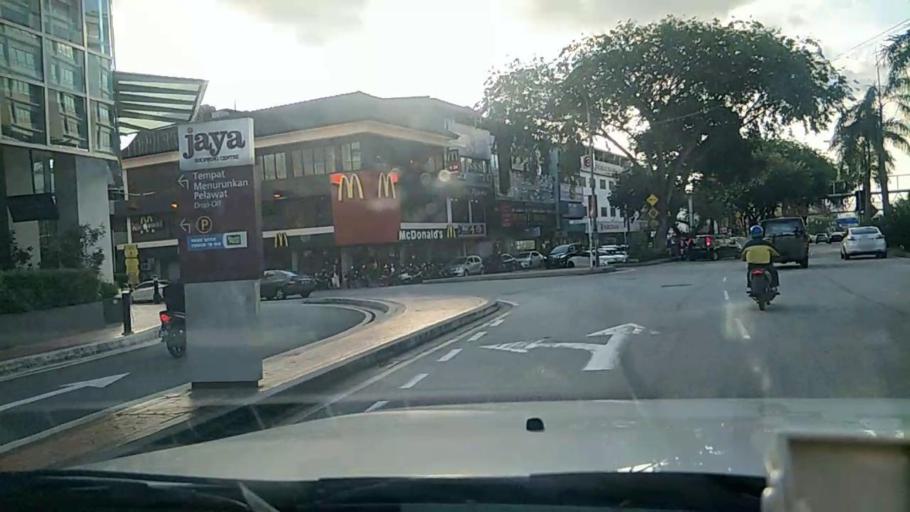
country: MY
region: Selangor
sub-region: Petaling
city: Petaling Jaya
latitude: 3.1095
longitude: 101.6375
